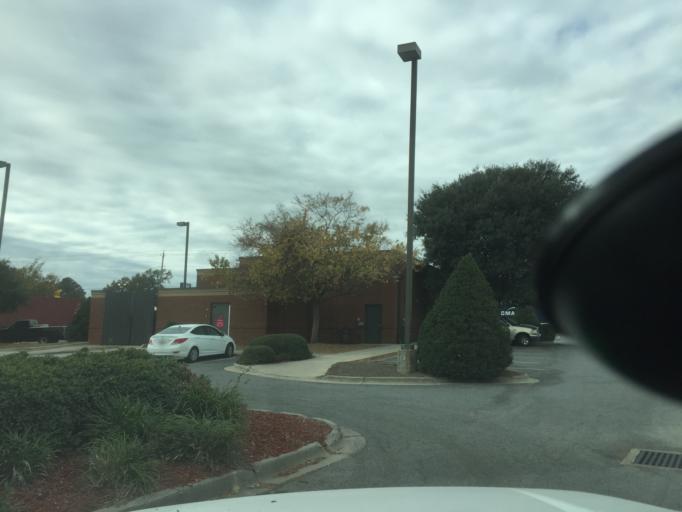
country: US
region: Georgia
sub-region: Chatham County
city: Garden City
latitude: 32.1266
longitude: -81.1686
